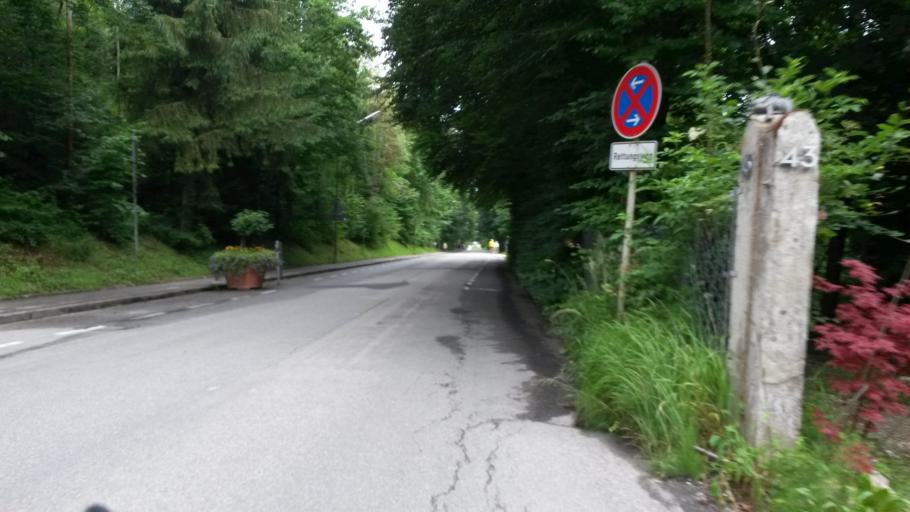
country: DE
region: Bavaria
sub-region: Upper Bavaria
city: Prien am Chiemsee
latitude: 47.8531
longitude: 12.3670
